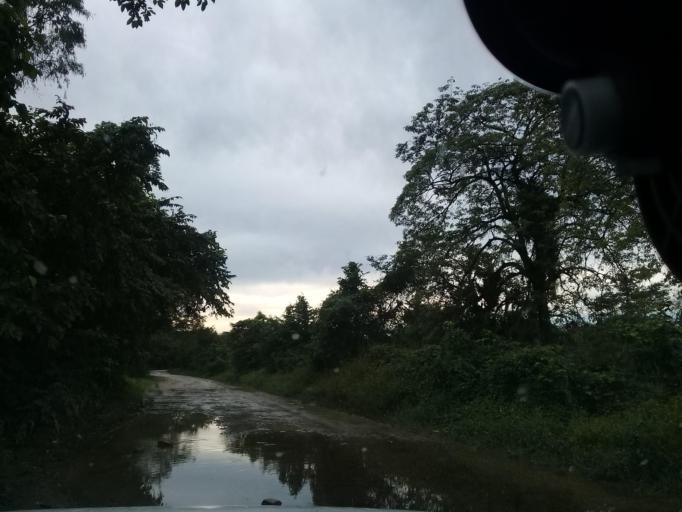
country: MX
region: Hidalgo
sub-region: Huejutla de Reyes
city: Chalahuiyapa
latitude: 21.1579
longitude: -98.3703
